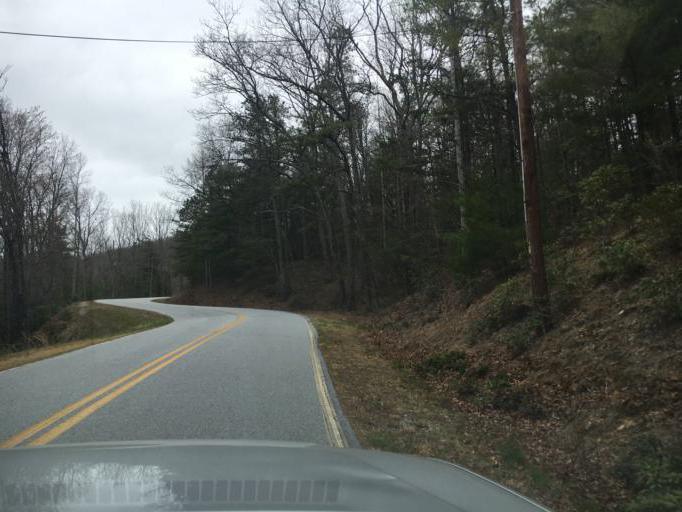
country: US
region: North Carolina
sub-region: Henderson County
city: East Flat Rock
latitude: 35.2514
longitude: -82.4159
